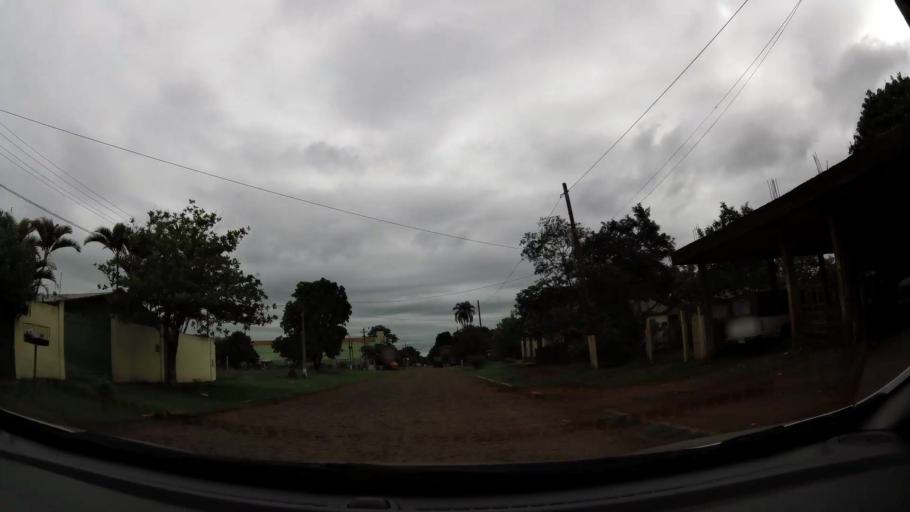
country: PY
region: Alto Parana
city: Ciudad del Este
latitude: -25.4029
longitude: -54.6435
